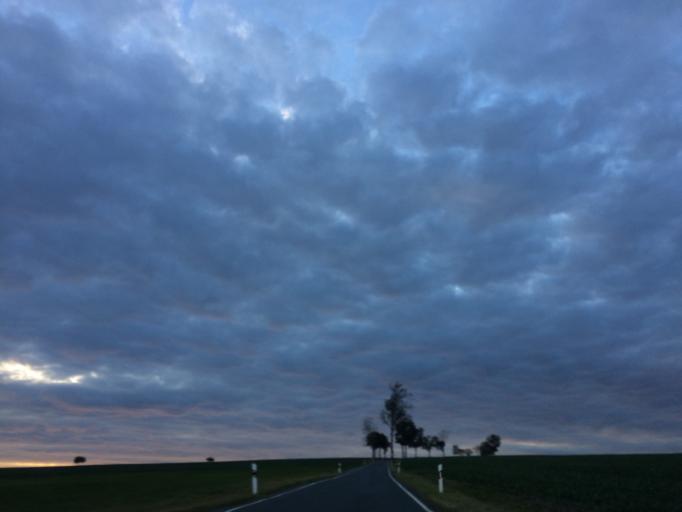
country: DE
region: Thuringia
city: Moxa
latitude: 50.6363
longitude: 11.6383
